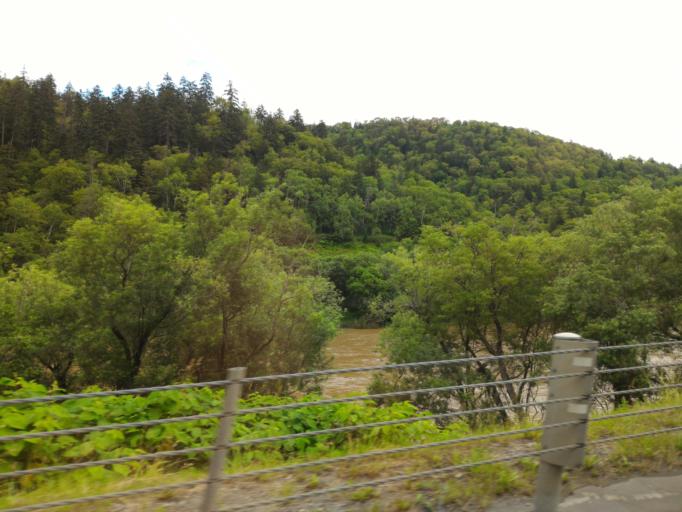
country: JP
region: Hokkaido
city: Nayoro
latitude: 44.7258
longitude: 142.2334
